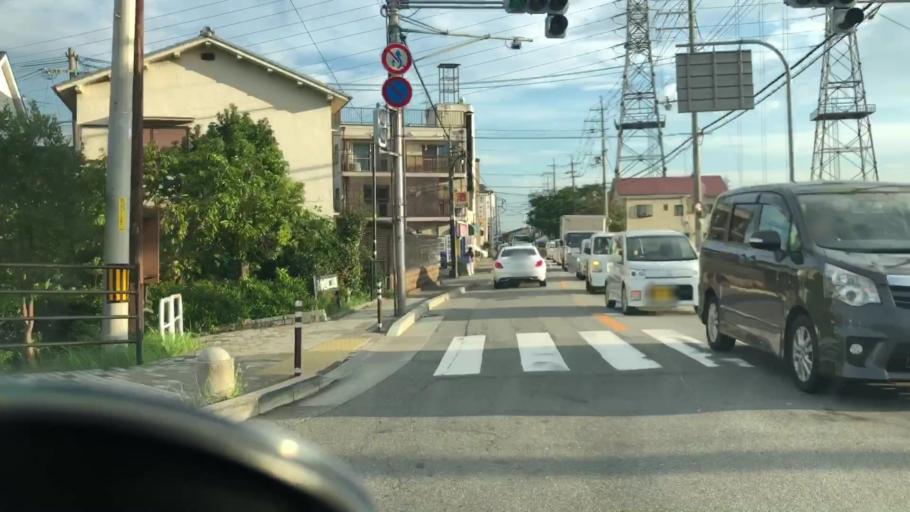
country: JP
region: Hyogo
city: Takarazuka
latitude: 34.7880
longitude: 135.3690
